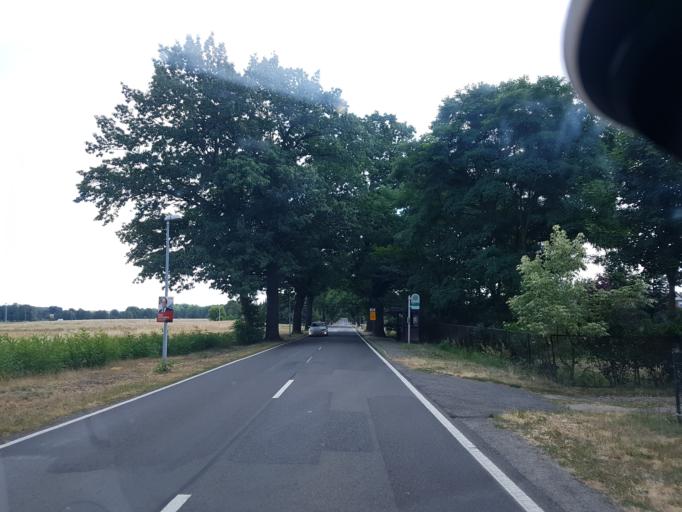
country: DE
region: Brandenburg
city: Drebkau
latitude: 51.6622
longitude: 14.2010
